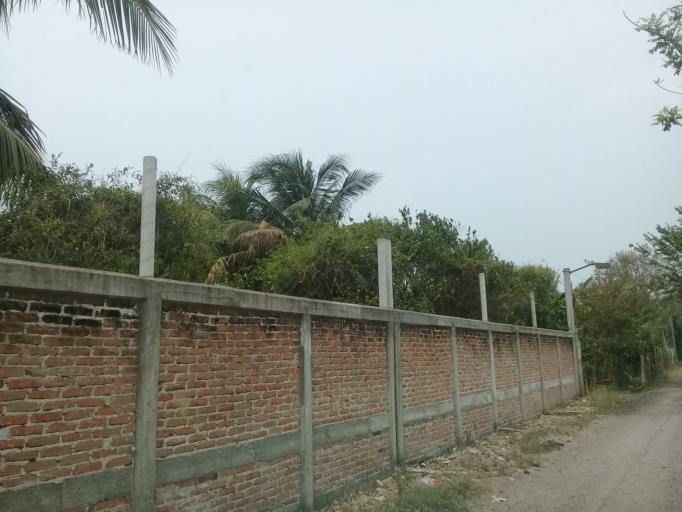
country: MX
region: Veracruz
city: Jamapa
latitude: 18.9556
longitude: -96.1958
